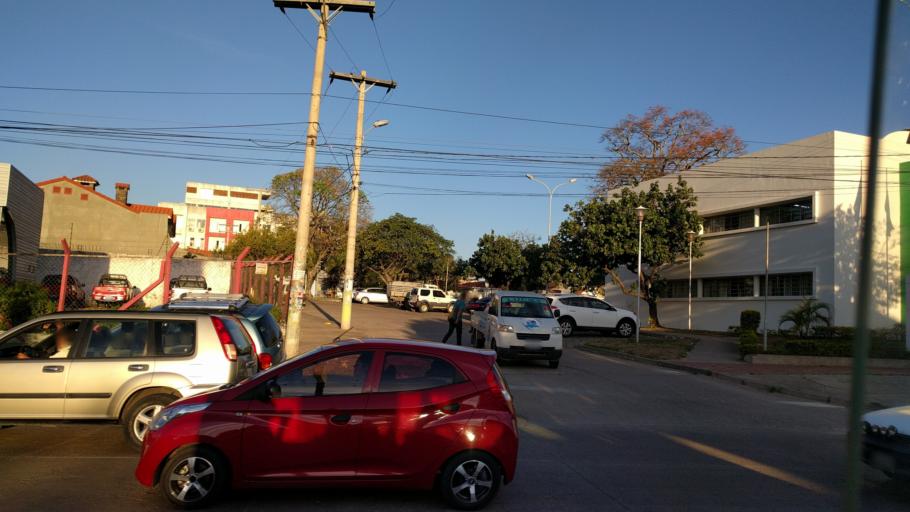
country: BO
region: Santa Cruz
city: Santa Cruz de la Sierra
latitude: -17.7701
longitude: -63.2020
